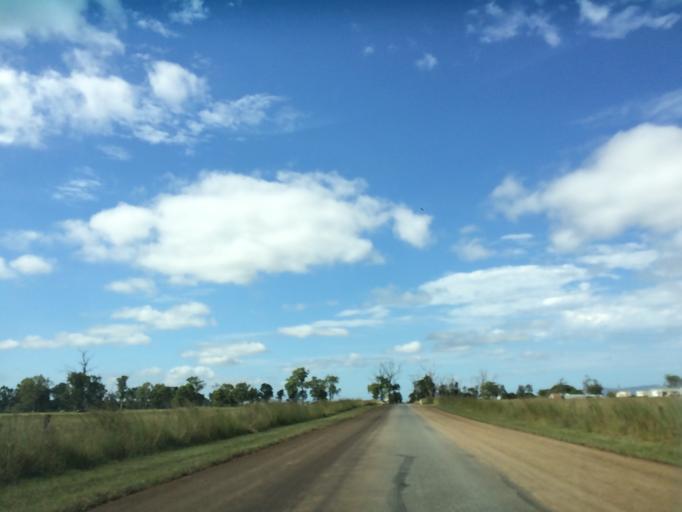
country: AU
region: Queensland
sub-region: Logan
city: Cedar Vale
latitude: -27.8758
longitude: 152.9561
